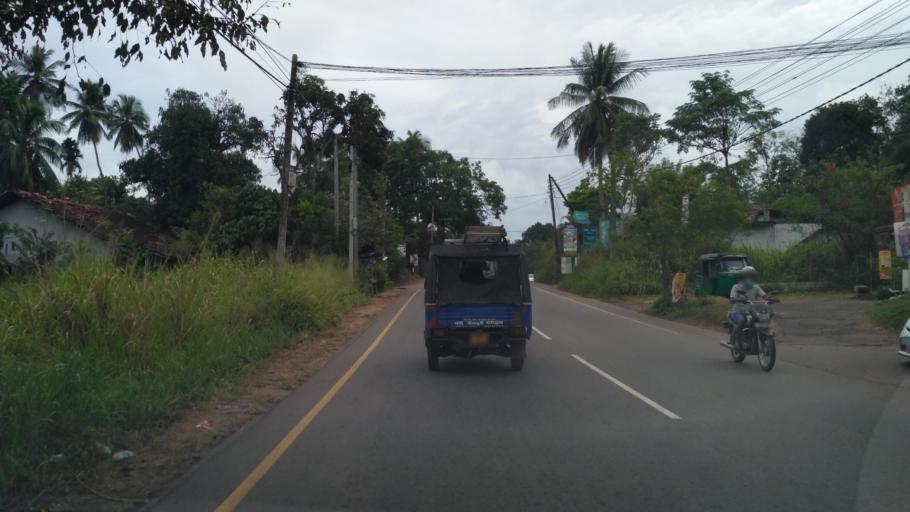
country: LK
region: North Western
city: Kuliyapitiya
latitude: 7.3269
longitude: 80.0468
